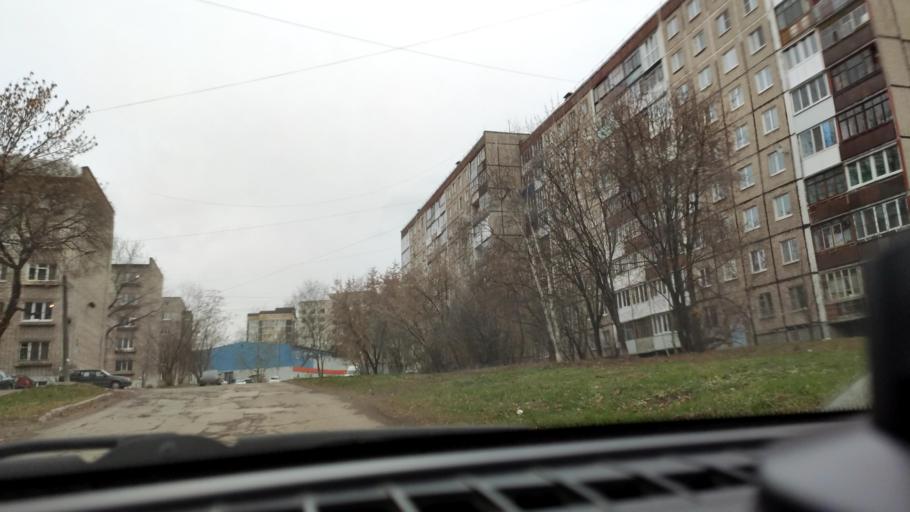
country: RU
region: Perm
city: Perm
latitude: 58.0214
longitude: 56.3015
